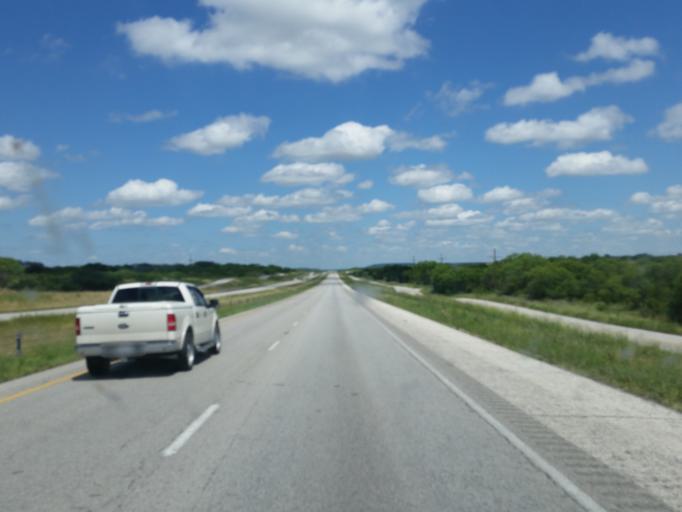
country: US
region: Texas
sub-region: Callahan County
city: Baird
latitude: 32.3845
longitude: -99.2890
